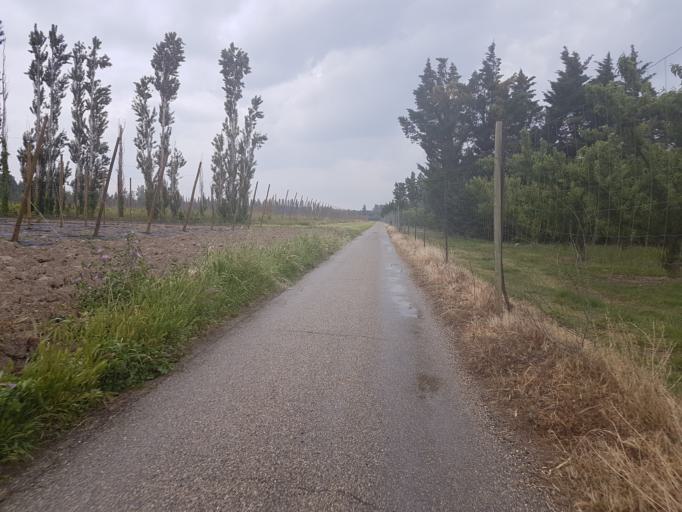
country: FR
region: Languedoc-Roussillon
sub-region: Departement du Gard
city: Villeneuve-les-Avignon
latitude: 43.9729
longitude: 4.8224
